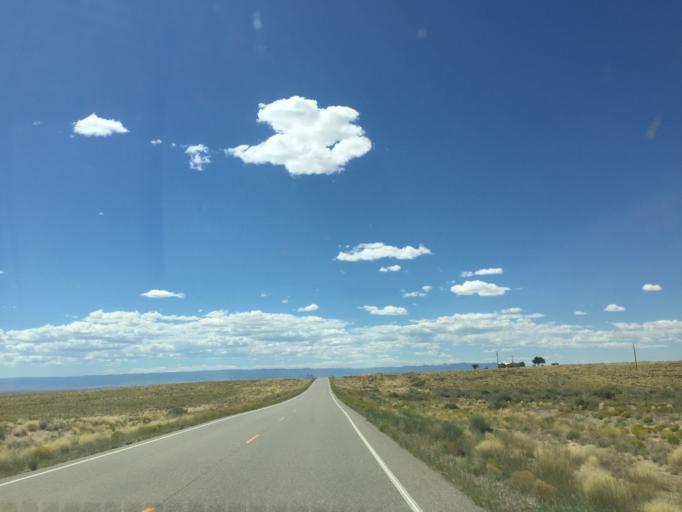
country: US
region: New Mexico
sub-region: San Juan County
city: Upper Fruitland
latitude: 36.4278
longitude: -108.3908
